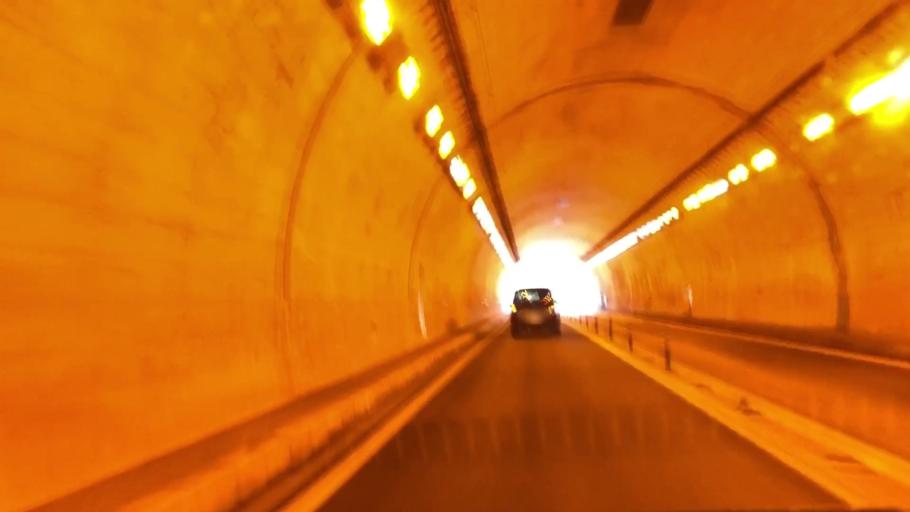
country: JP
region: Saga Prefecture
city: Ureshinomachi-shimojuku
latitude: 33.1566
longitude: 129.9061
